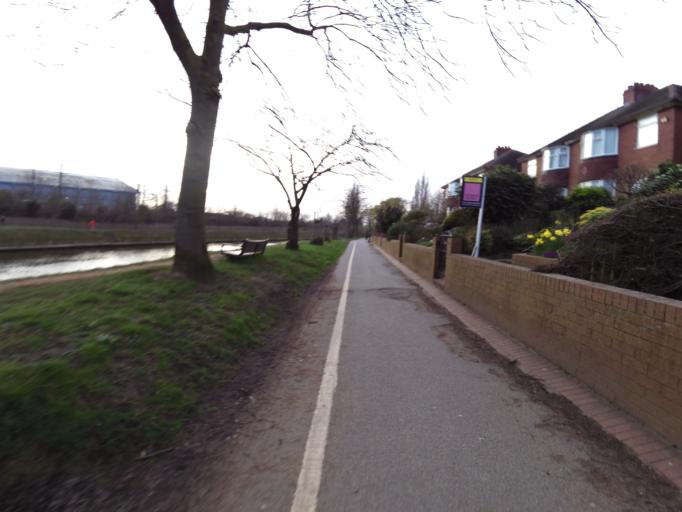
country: GB
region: England
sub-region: City of York
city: York
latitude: 53.9617
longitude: -1.0939
